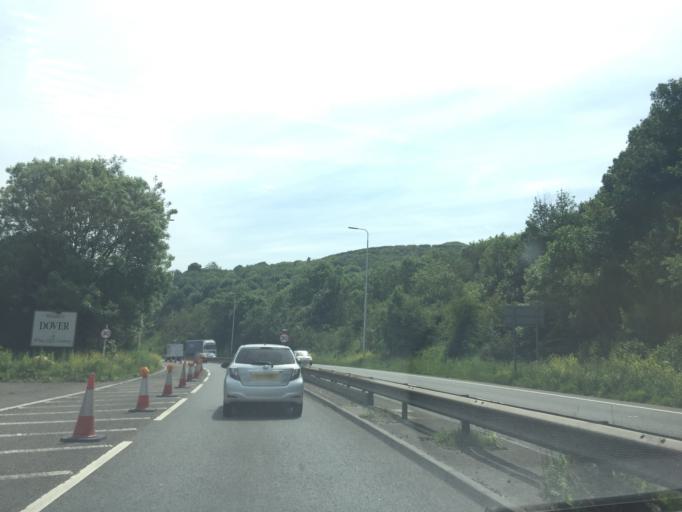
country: GB
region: England
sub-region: Kent
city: Dover
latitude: 51.1319
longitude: 1.3289
